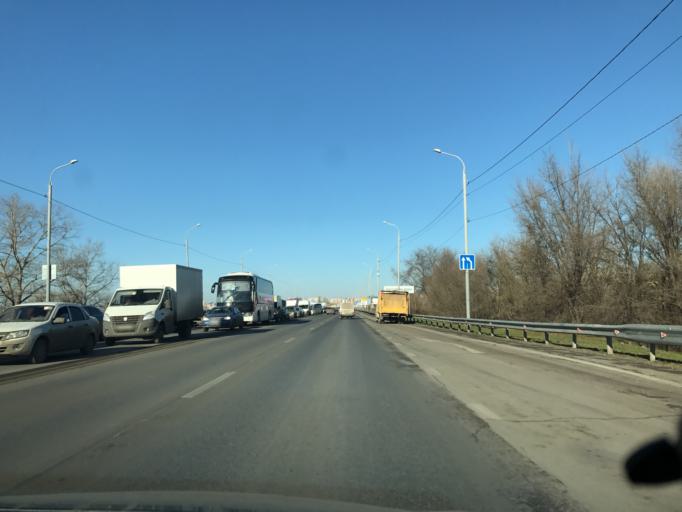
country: RU
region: Rostov
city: Bataysk
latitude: 47.1844
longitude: 39.7378
